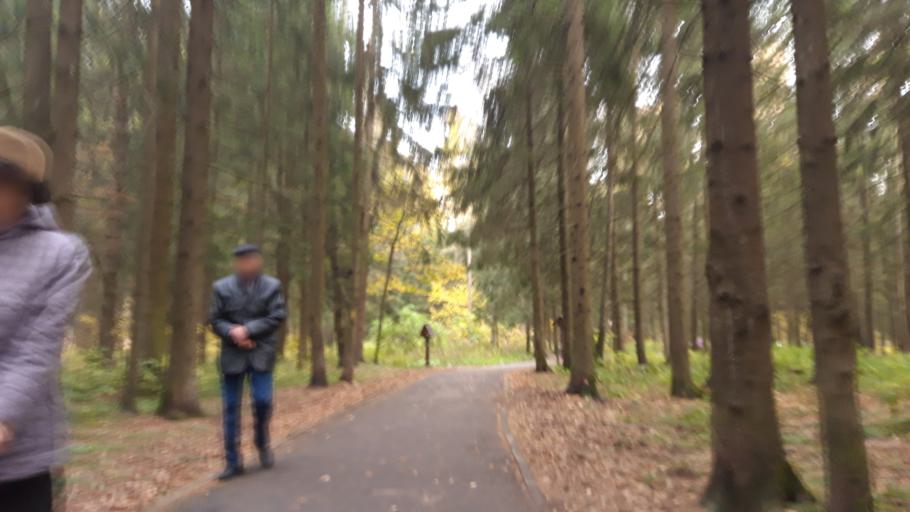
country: RU
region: Moscow
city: Zelenograd
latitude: 55.9975
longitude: 37.1709
